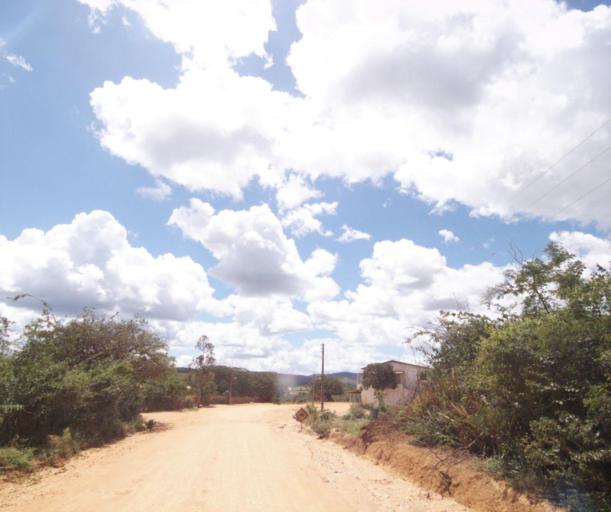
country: BR
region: Bahia
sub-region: Pocoes
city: Pocoes
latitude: -14.3534
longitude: -40.5930
